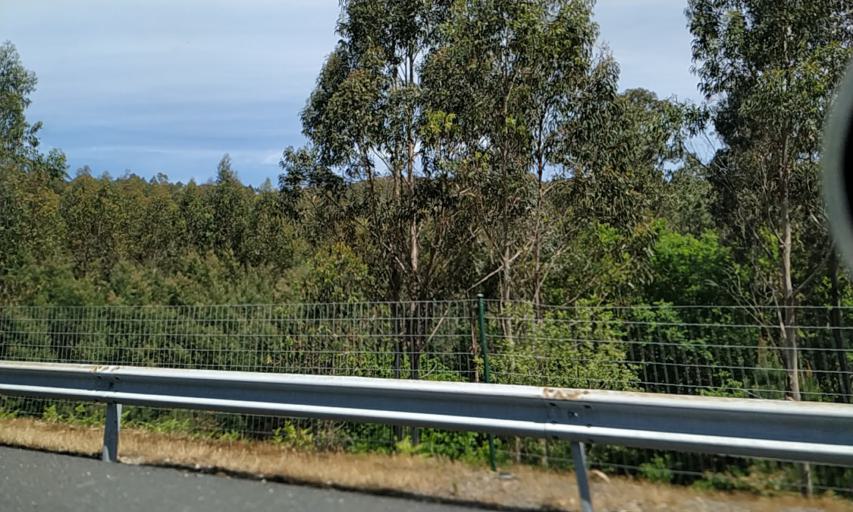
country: ES
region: Galicia
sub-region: Provincia da Coruna
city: Padron
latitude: 42.7789
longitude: -8.6422
